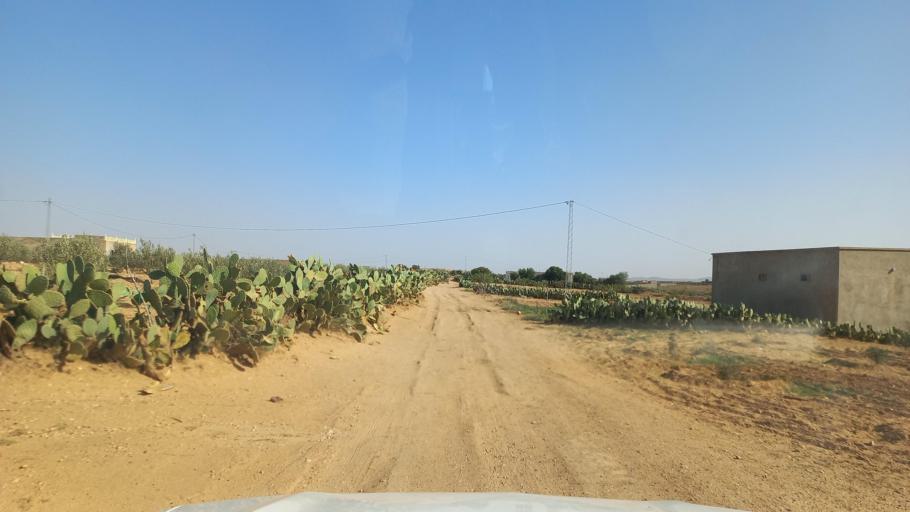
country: TN
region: Al Qasrayn
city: Sbiba
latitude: 35.3212
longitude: 9.0202
